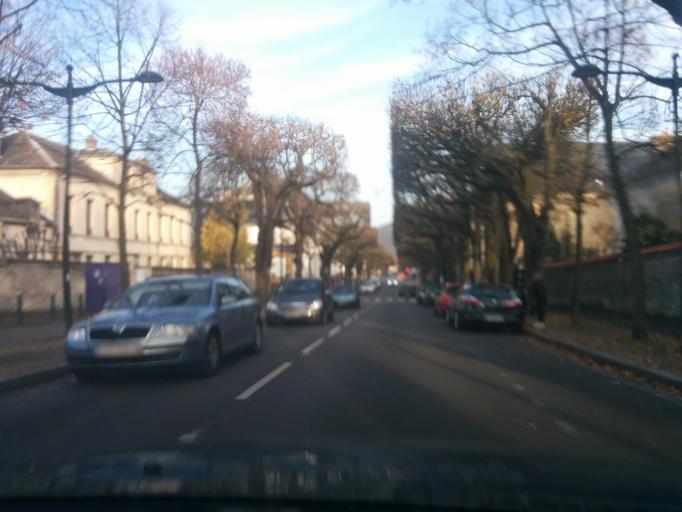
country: FR
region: Haute-Normandie
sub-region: Departement de l'Eure
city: Vernon
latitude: 49.0897
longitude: 1.4828
